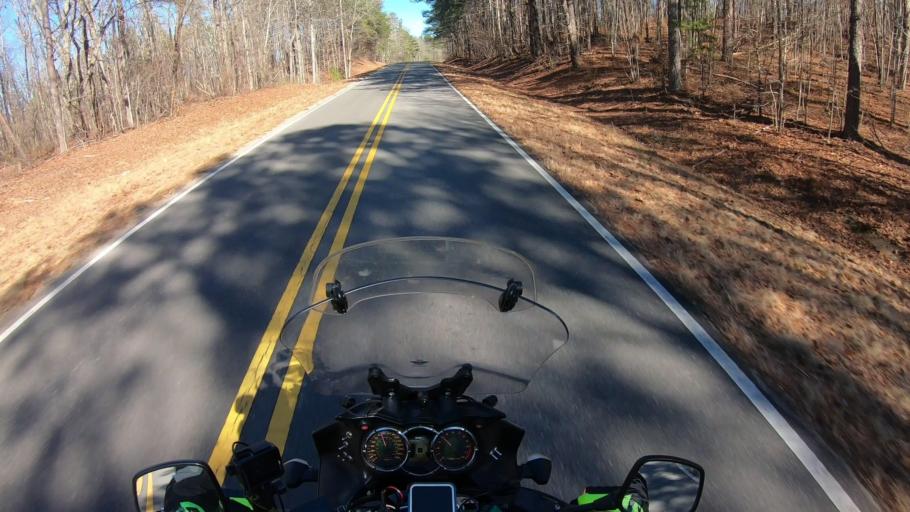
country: US
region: Alabama
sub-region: Calhoun County
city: Choccolocco
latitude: 33.5701
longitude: -85.6981
